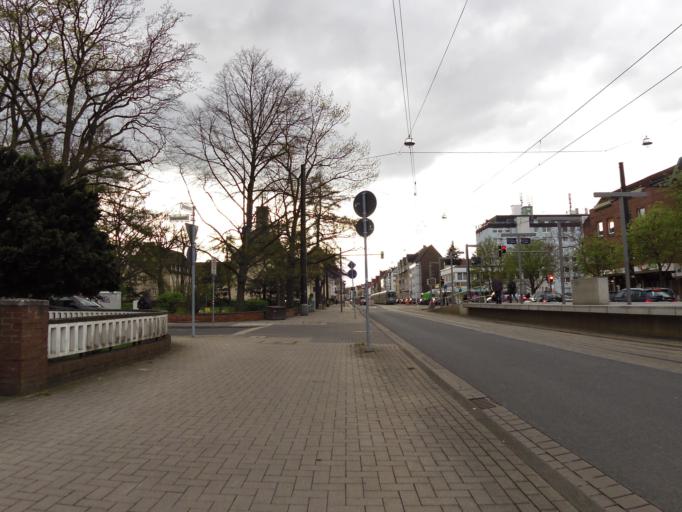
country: DE
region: Lower Saxony
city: Laatzen
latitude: 52.3715
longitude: 9.7934
